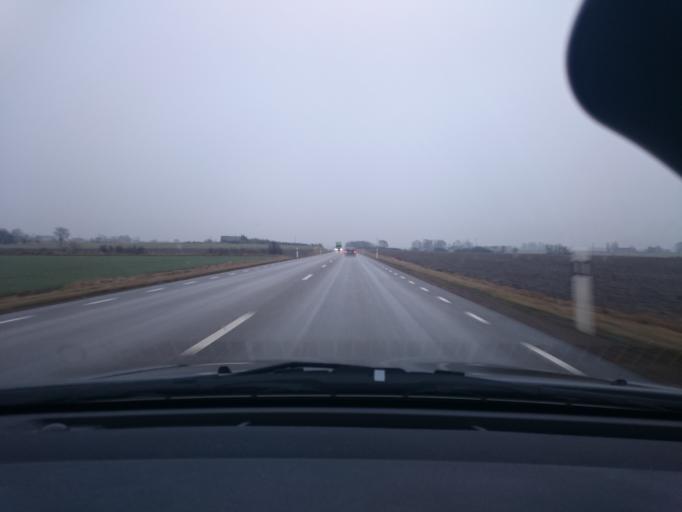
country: SE
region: Skane
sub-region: Bastads Kommun
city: Forslov
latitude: 56.3294
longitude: 12.8208
